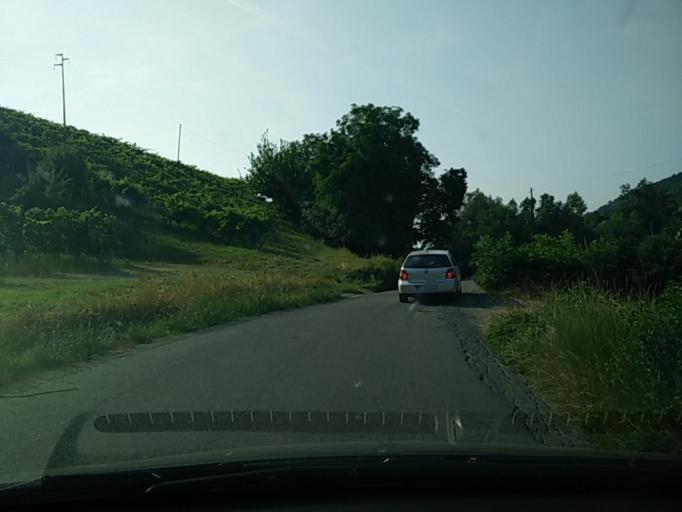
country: IT
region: Lombardy
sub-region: Provincia di Pavia
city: Susella
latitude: 44.9389
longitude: 9.1155
